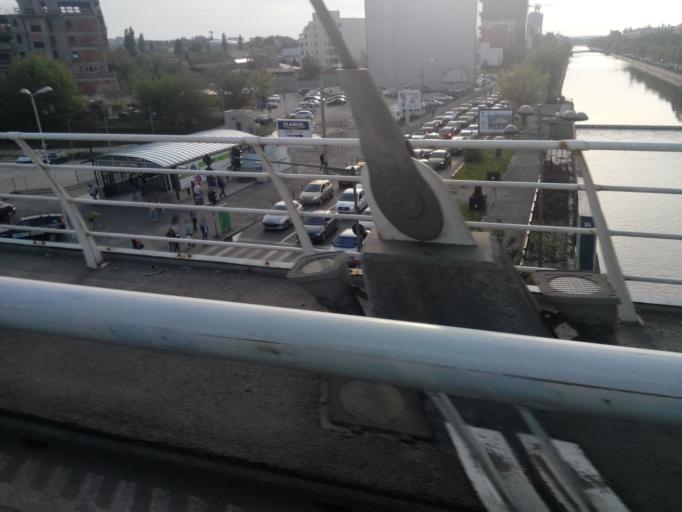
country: RO
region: Bucuresti
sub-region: Municipiul Bucuresti
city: Bucuresti
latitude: 44.4432
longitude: 26.0606
